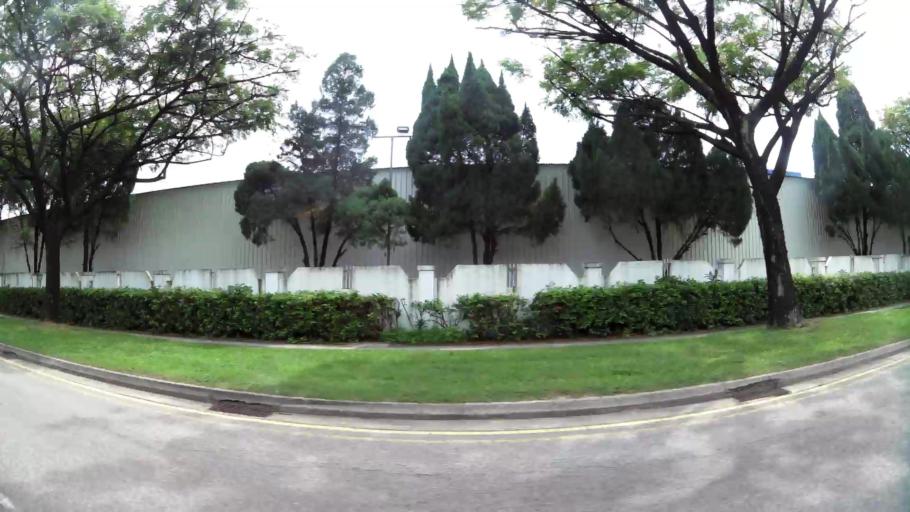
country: MY
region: Johor
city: Johor Bahru
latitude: 1.3220
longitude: 103.6719
